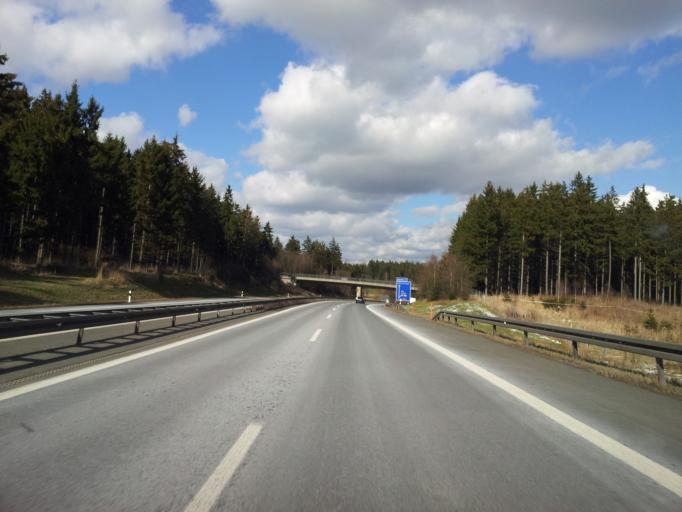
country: DE
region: Bavaria
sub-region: Upper Franconia
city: Koditz
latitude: 50.3387
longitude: 11.8181
